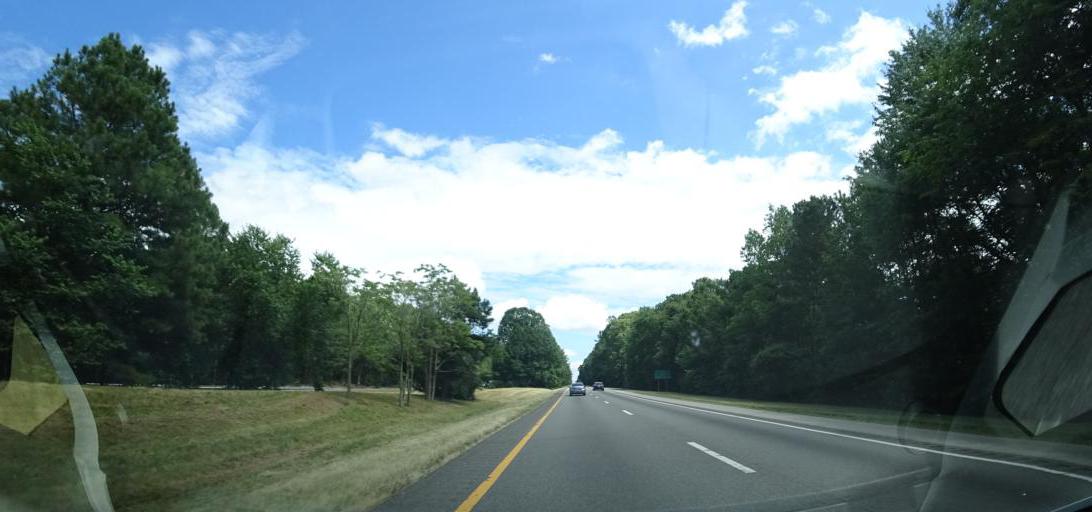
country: US
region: Virginia
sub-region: James City County
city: Williamsburg
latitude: 37.3652
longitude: -76.7459
